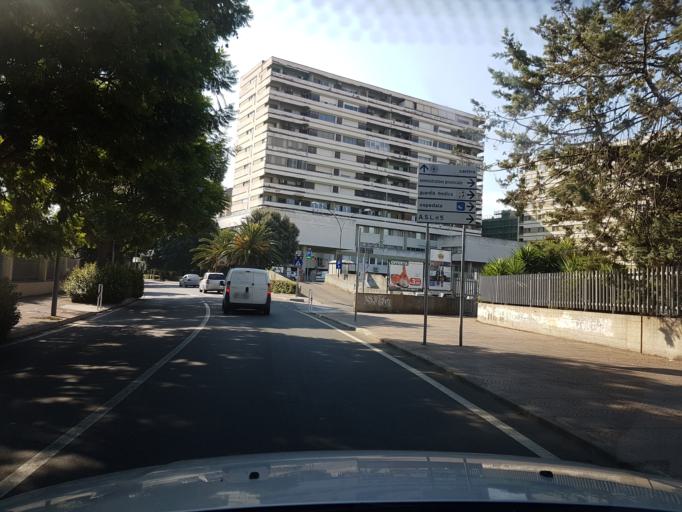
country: IT
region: Sardinia
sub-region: Provincia di Oristano
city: Oristano
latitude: 39.9025
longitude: 8.5887
